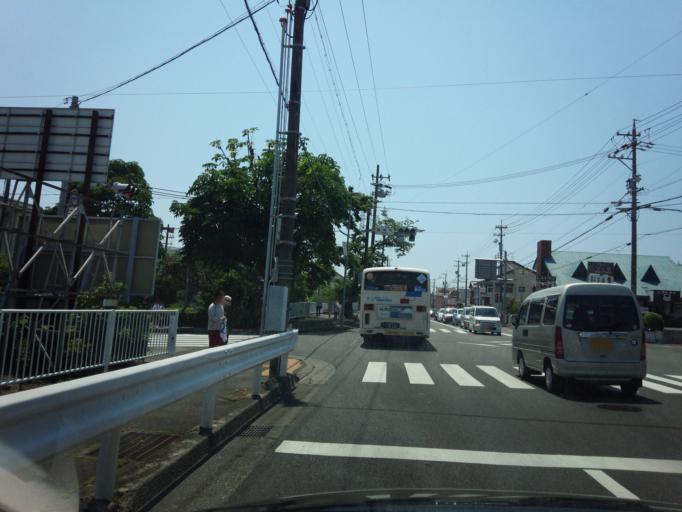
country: JP
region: Shizuoka
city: Shizuoka-shi
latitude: 34.9907
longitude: 138.4858
